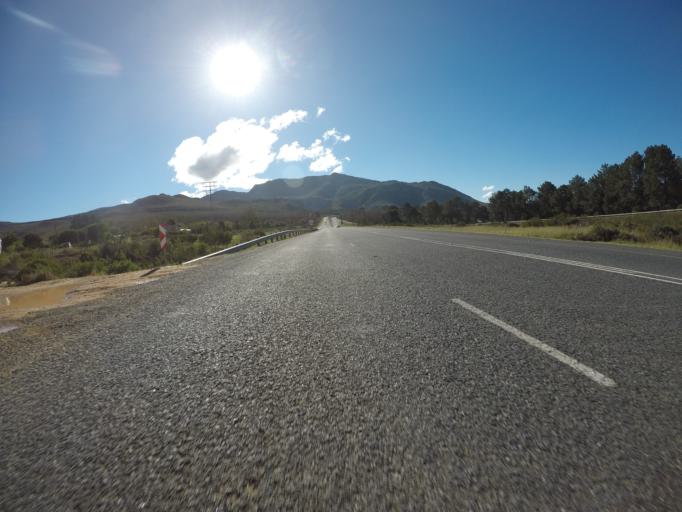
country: ZA
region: Western Cape
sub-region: Overberg District Municipality
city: Grabouw
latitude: -34.2298
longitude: 19.1877
